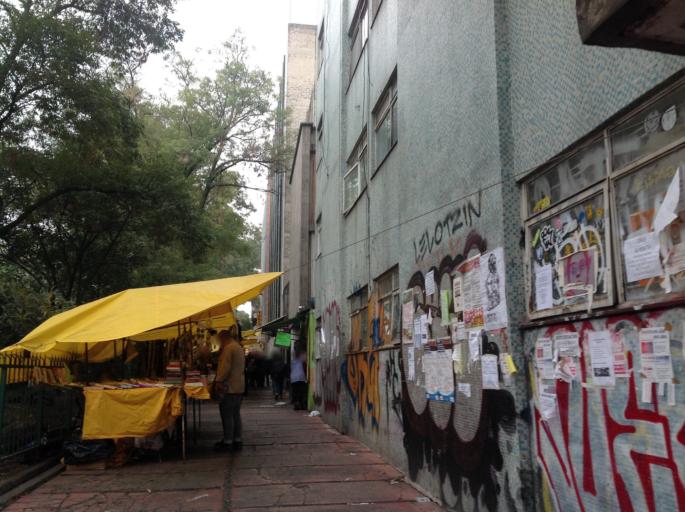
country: MX
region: Mexico City
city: Coyoacan
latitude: 19.3345
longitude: -99.1789
